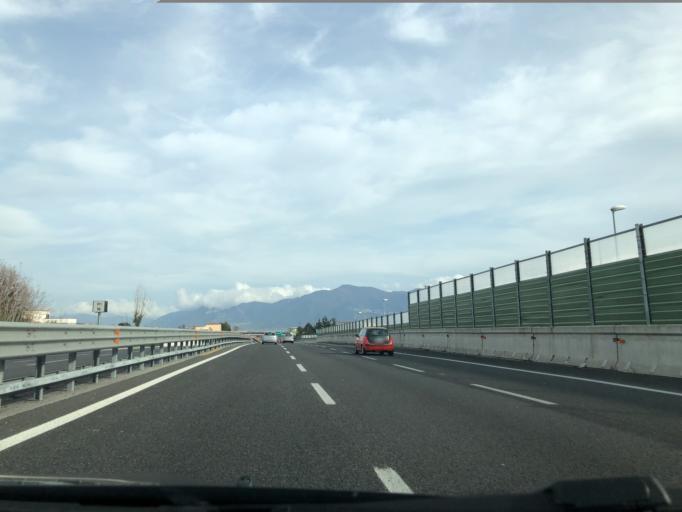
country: IT
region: Campania
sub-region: Provincia di Napoli
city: Trecase
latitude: 40.7688
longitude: 14.4226
